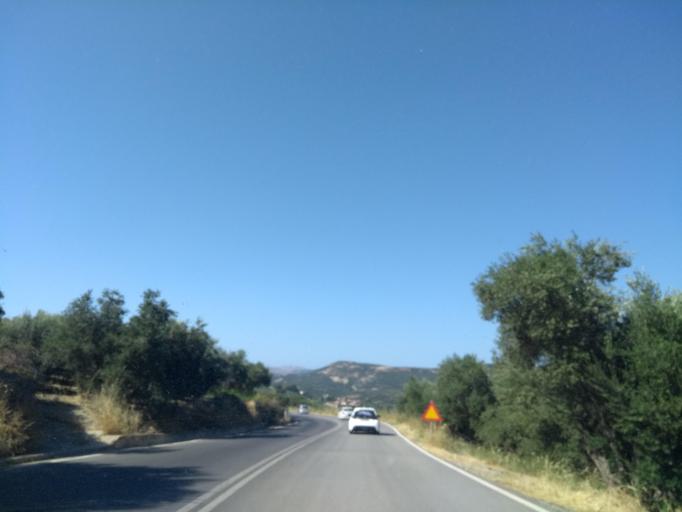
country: GR
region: Crete
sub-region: Nomos Chanias
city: Kissamos
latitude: 35.4388
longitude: 23.6912
